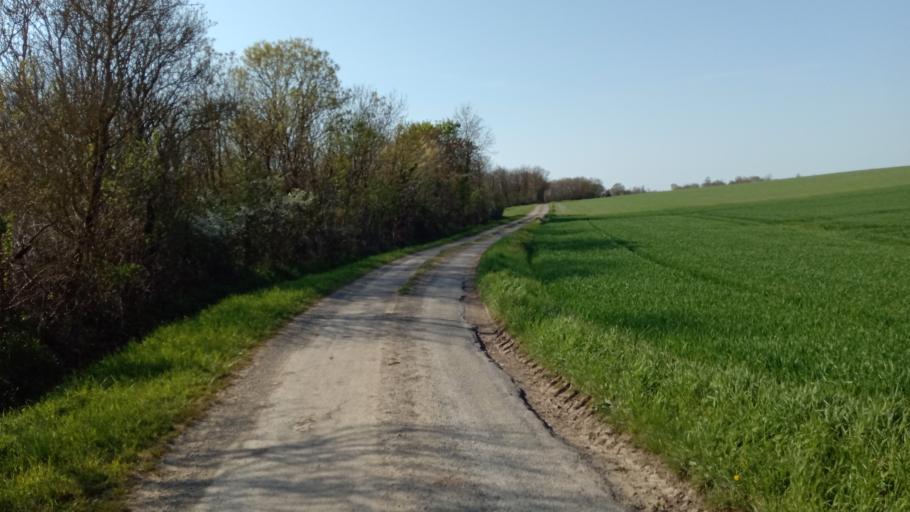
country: FR
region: Poitou-Charentes
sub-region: Departement de la Charente-Maritime
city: Verines
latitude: 46.1609
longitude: -0.9372
